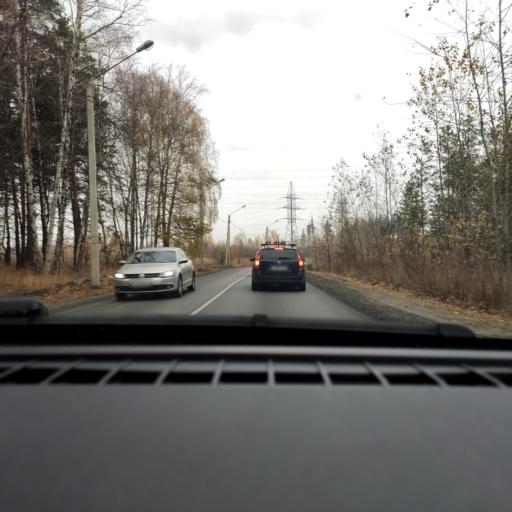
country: RU
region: Voronezj
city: Somovo
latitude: 51.7247
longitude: 39.3187
